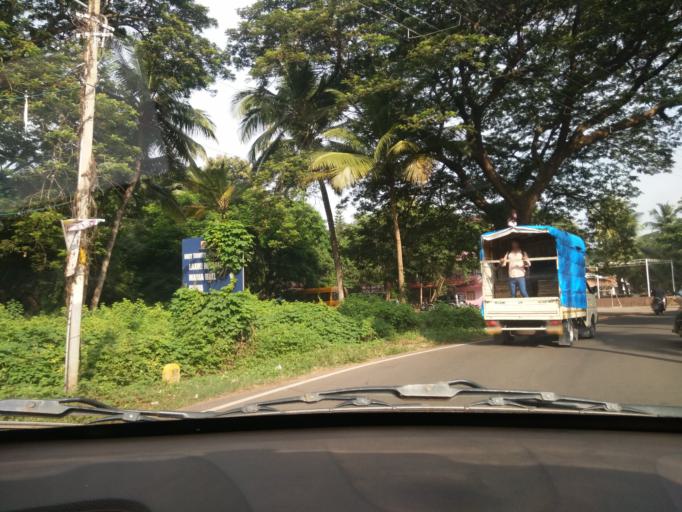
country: IN
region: Goa
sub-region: South Goa
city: Benaulim
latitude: 15.2520
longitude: 73.9344
